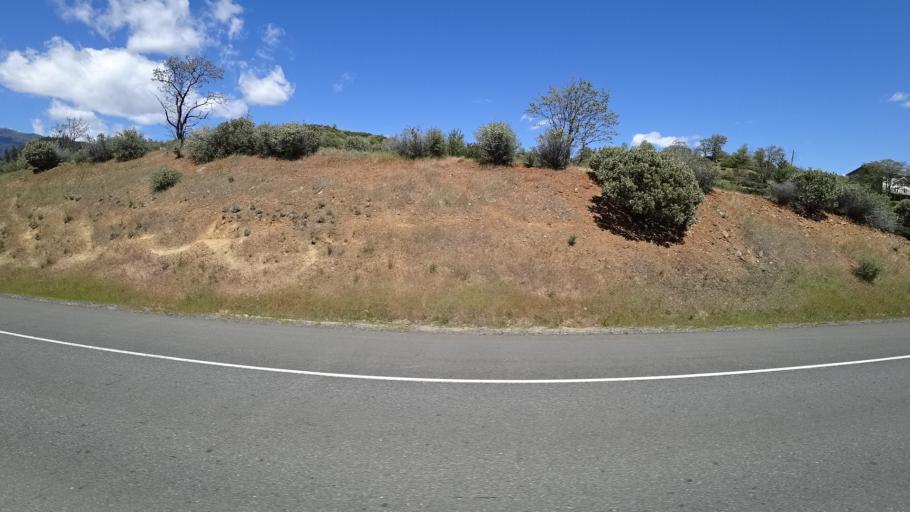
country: US
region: California
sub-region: Trinity County
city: Weaverville
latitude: 40.7376
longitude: -122.9656
